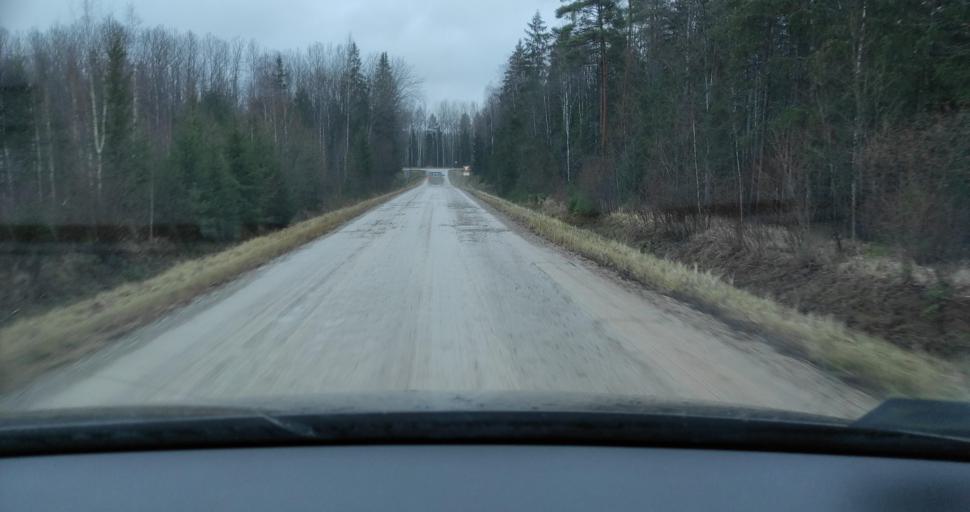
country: LV
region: Skrunda
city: Skrunda
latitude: 56.5781
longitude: 22.1388
